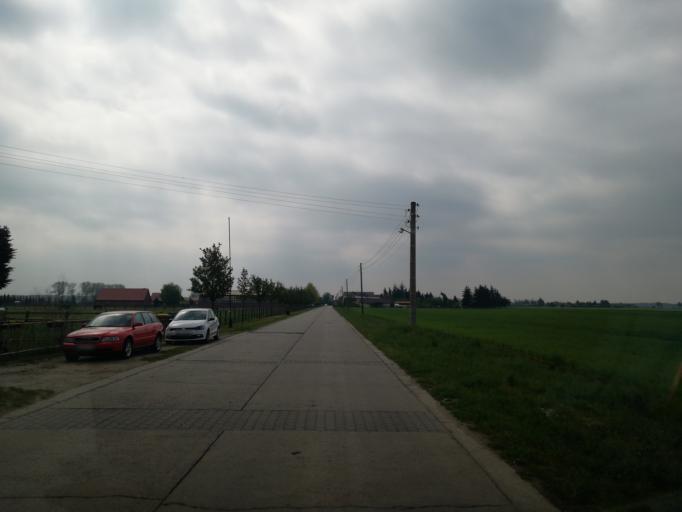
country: DE
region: Saxony
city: Beilrode
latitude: 51.6511
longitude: 13.1164
